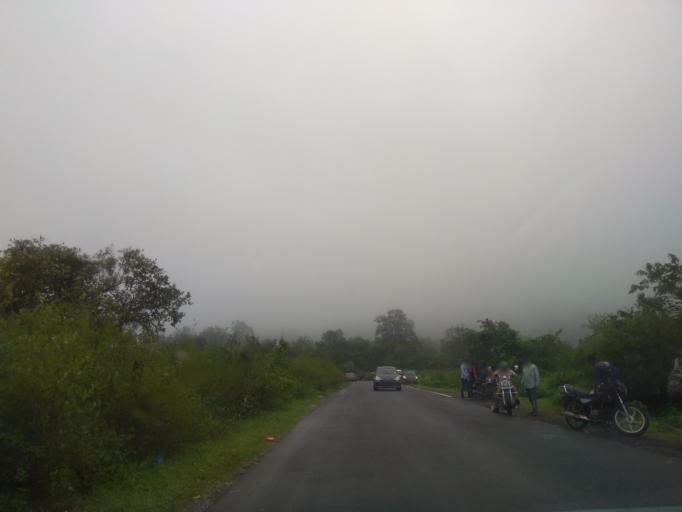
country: IN
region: Maharashtra
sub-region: Raigarh
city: Indapur
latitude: 18.4910
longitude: 73.4252
